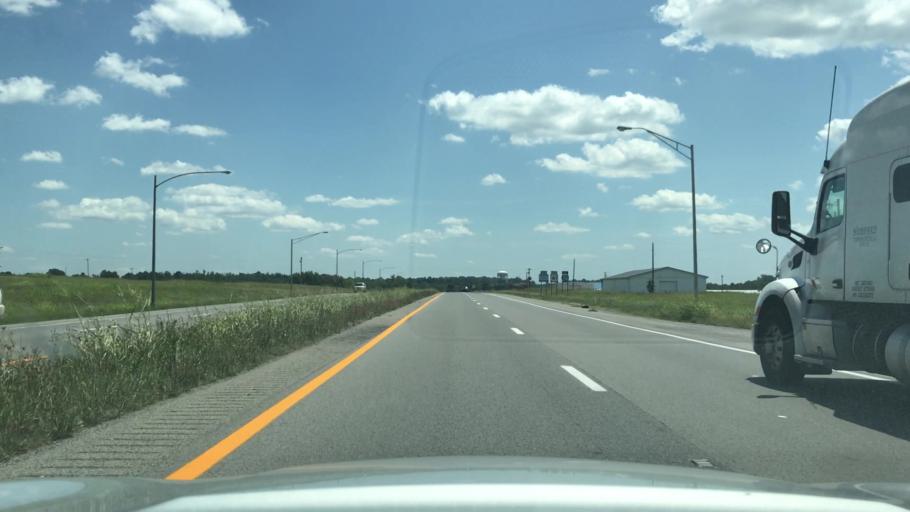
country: US
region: Kentucky
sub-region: Christian County
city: Hopkinsville
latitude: 36.8935
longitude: -87.4692
